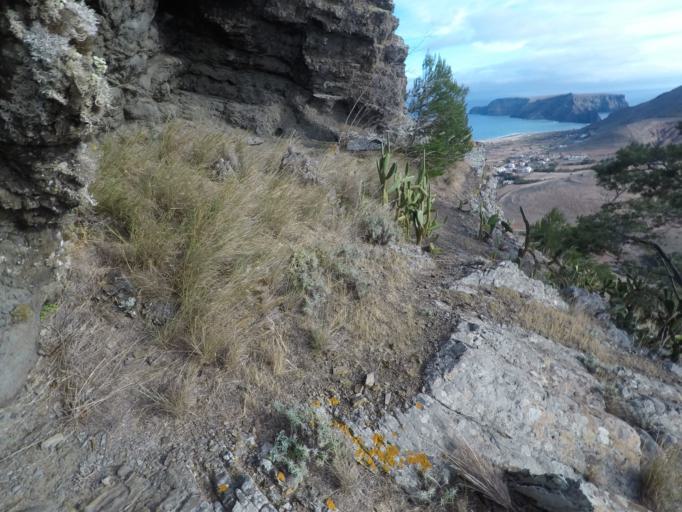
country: PT
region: Madeira
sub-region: Porto Santo
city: Vila de Porto Santo
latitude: 33.0423
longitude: -16.3708
